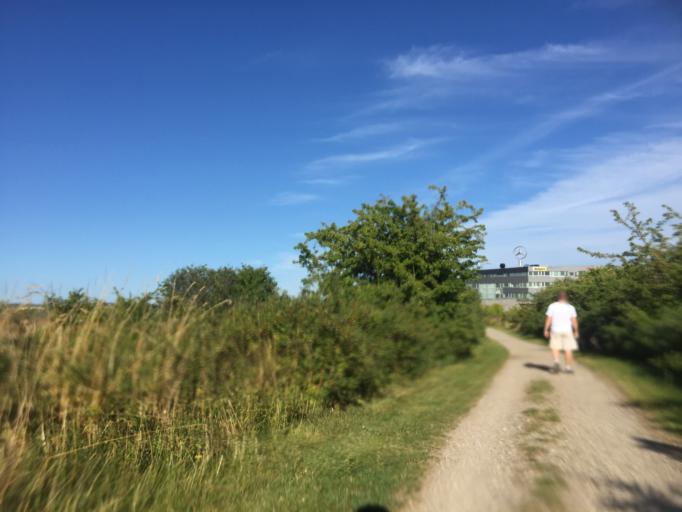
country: DK
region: Capital Region
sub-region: Tarnby Kommune
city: Tarnby
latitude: 55.6416
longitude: 12.5810
